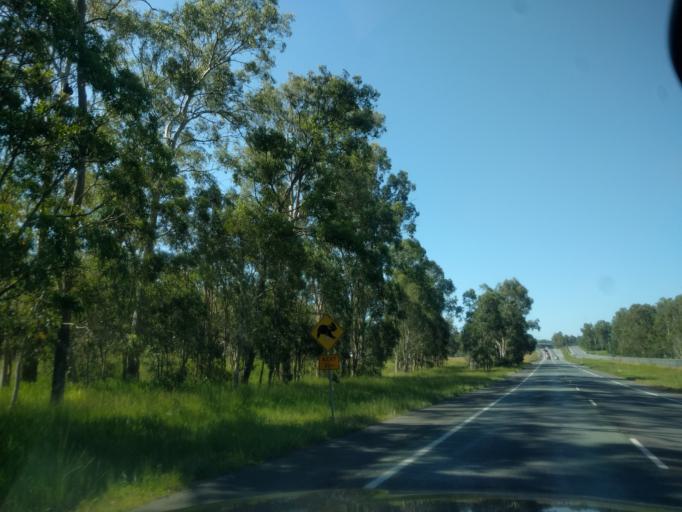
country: AU
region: Queensland
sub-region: Logan
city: Park Ridge South
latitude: -27.7327
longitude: 153.0286
